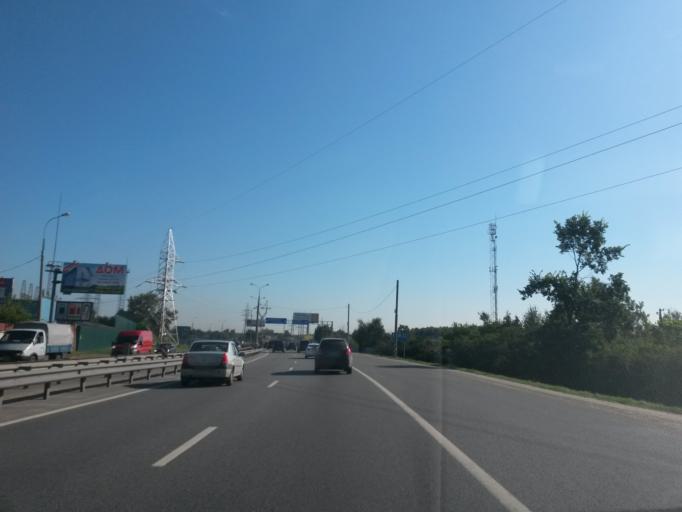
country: RU
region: Moskovskaya
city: Lesnyye Polyany
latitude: 55.9818
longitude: 37.8673
